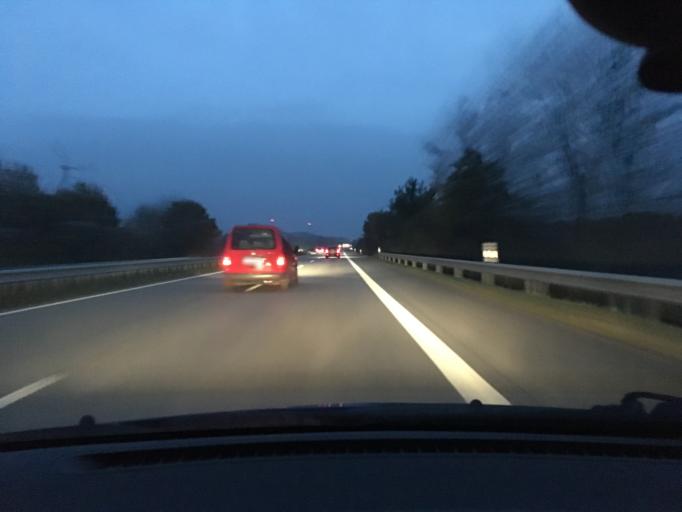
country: DE
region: Schleswig-Holstein
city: Bokelrehm
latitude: 54.0531
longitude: 9.3835
